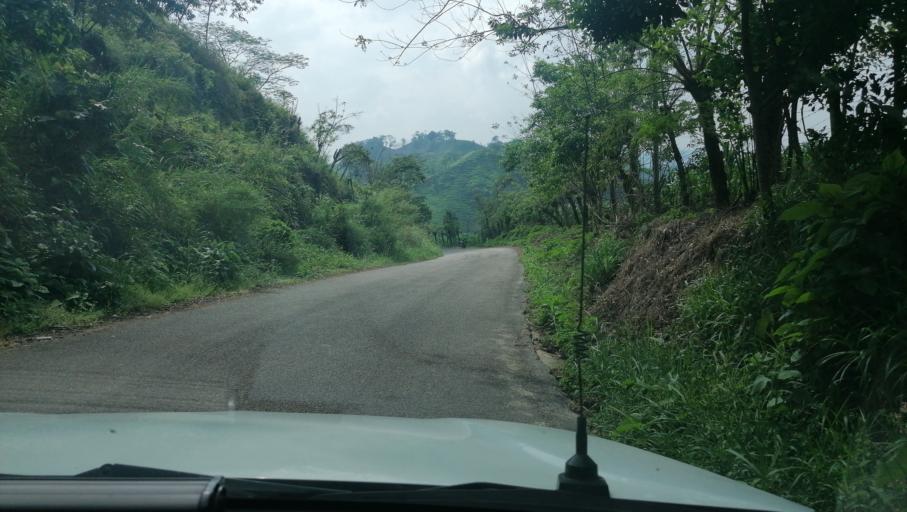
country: MX
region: Chiapas
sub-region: Francisco Leon
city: San Miguel la Sardina
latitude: 17.2371
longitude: -93.3238
